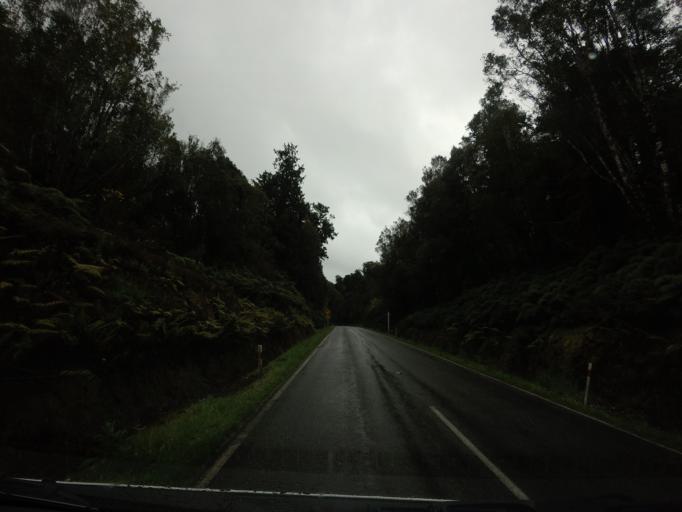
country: NZ
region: West Coast
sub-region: Westland District
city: Hokitika
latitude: -42.9817
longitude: 170.6824
